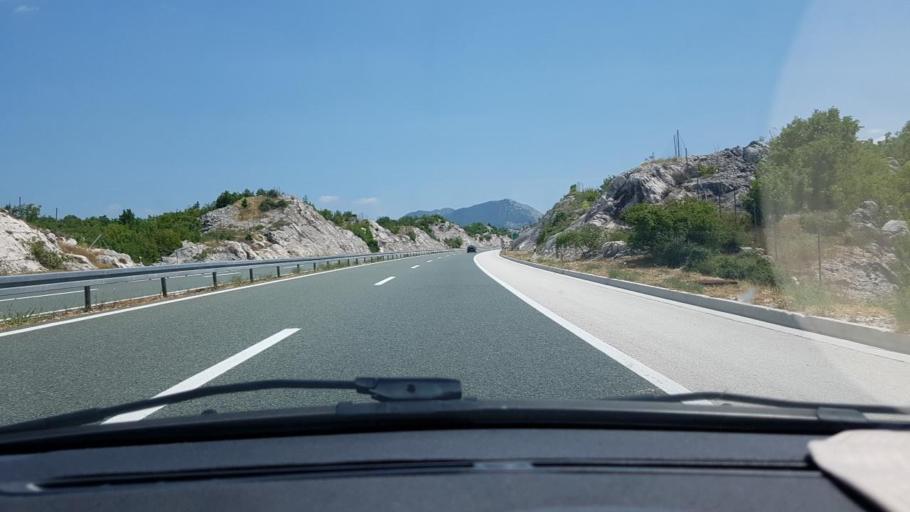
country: HR
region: Splitsko-Dalmatinska
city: Grubine
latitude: 43.3351
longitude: 17.1581
